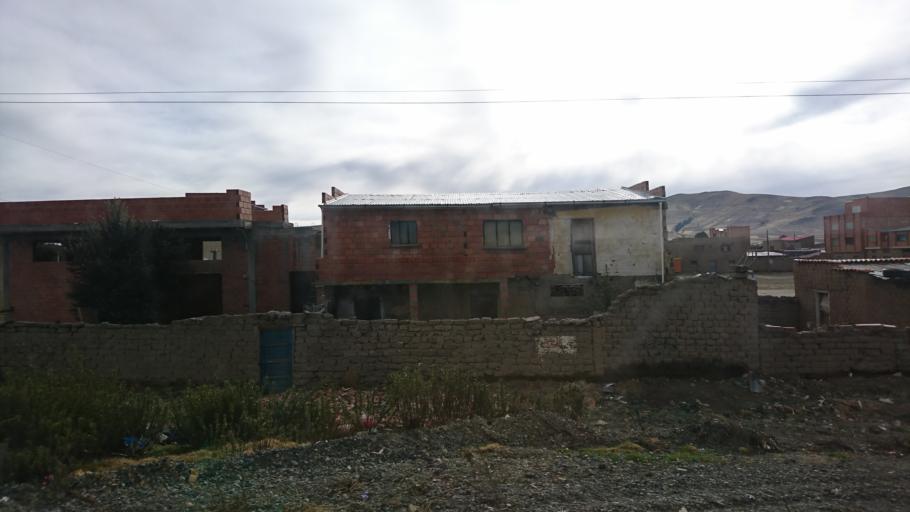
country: BO
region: La Paz
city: Batallas
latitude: -16.3767
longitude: -68.3801
